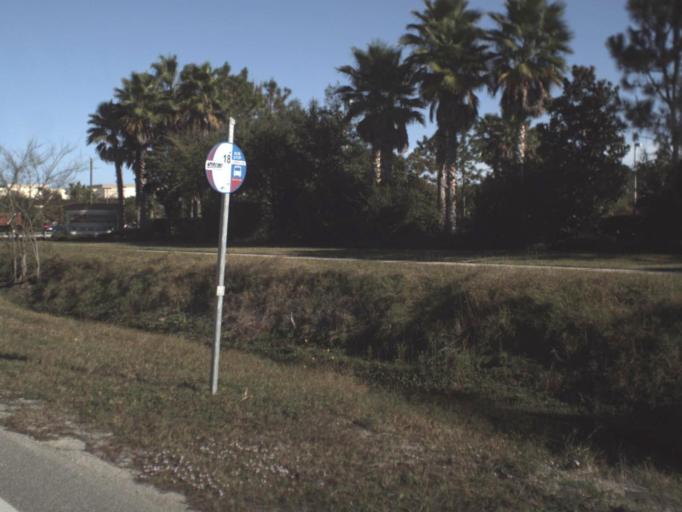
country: US
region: Florida
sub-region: Volusia County
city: Holly Hill
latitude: 29.2261
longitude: -81.0863
